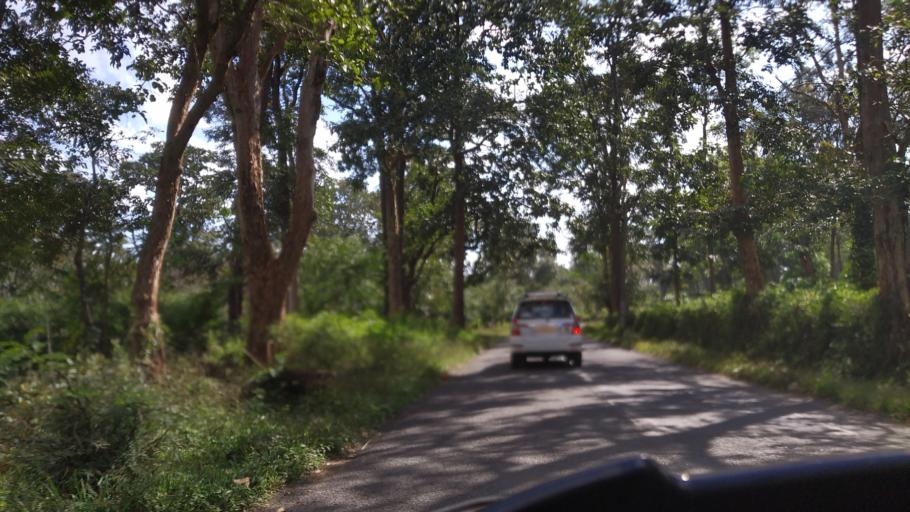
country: IN
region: Kerala
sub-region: Wayanad
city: Panamaram
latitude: 11.9507
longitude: 76.0654
